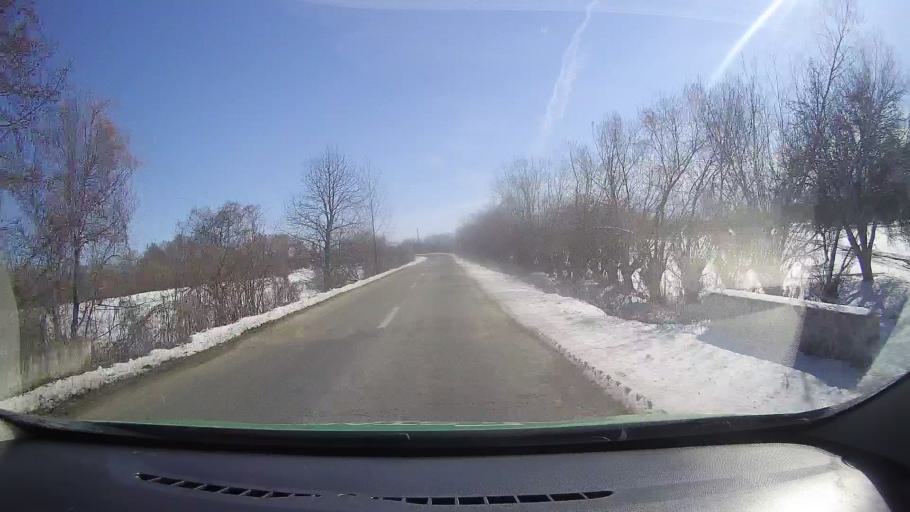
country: RO
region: Brasov
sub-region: Comuna Harseni
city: Harseni
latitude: 45.7315
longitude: 25.0212
